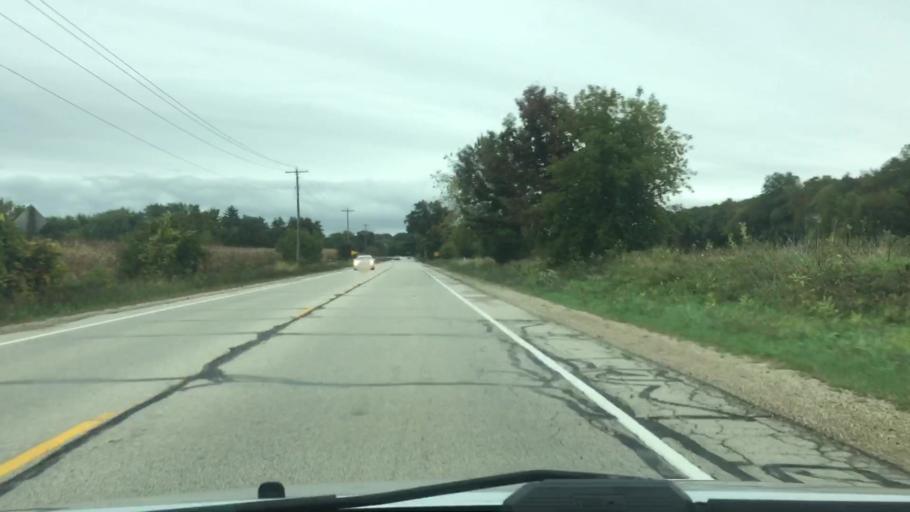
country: US
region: Wisconsin
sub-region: Jefferson County
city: Palmyra
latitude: 42.7939
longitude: -88.5630
